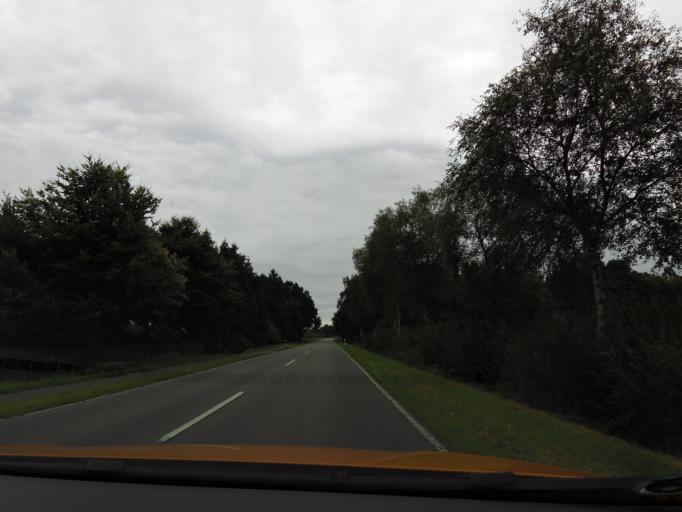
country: DE
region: Lower Saxony
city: Westerstede
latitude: 53.2414
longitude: 7.9836
